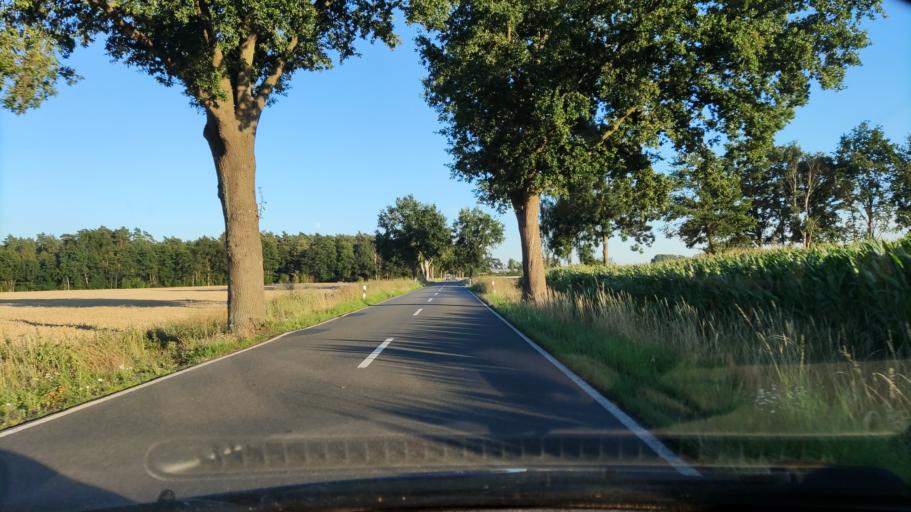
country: DE
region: Lower Saxony
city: Luechow
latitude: 53.0221
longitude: 11.1444
